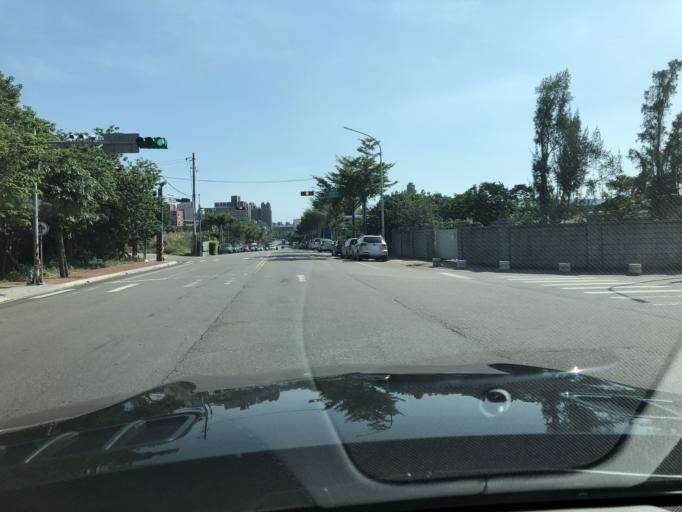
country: TW
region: Taiwan
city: Taoyuan City
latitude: 25.0660
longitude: 121.2909
